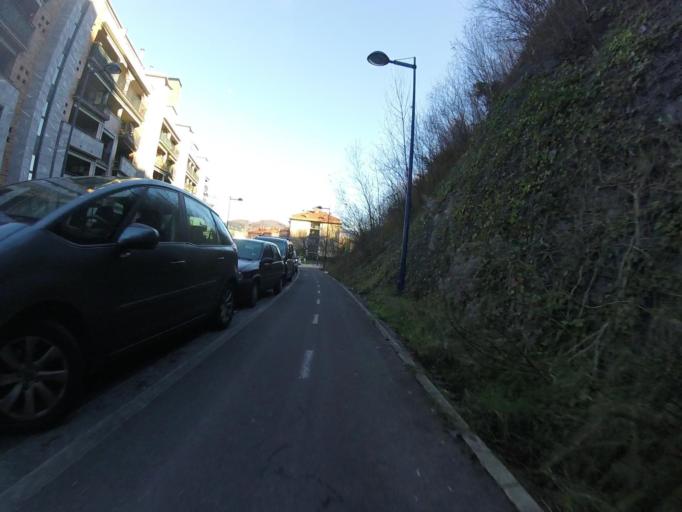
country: ES
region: Basque Country
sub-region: Provincia de Guipuzcoa
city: Errenteria
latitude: 43.3077
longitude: -1.8917
